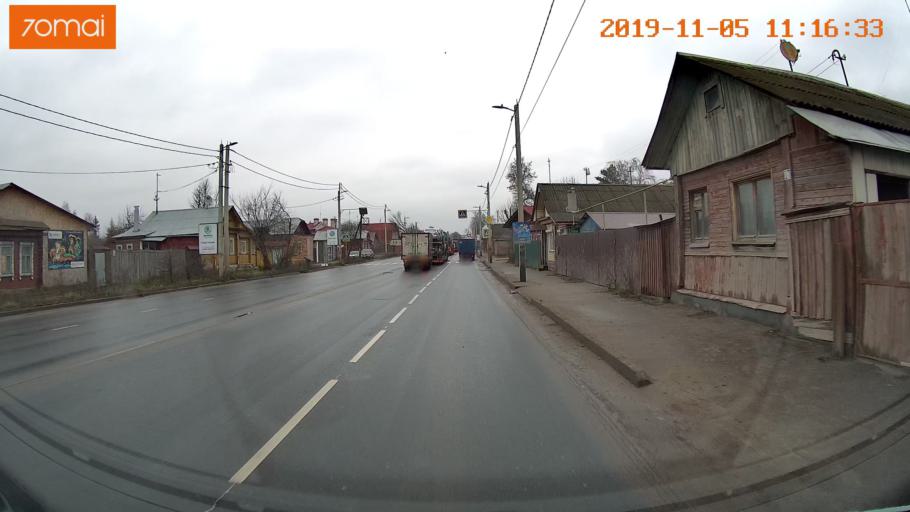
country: RU
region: Ivanovo
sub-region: Gorod Ivanovo
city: Ivanovo
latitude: 56.9859
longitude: 40.9533
